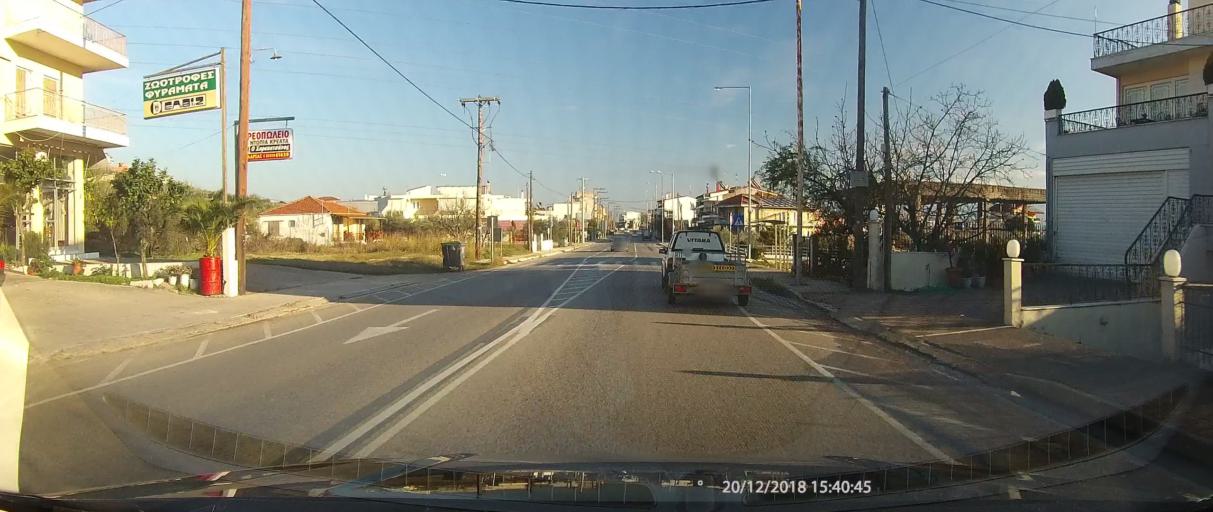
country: GR
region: Central Greece
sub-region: Nomos Fthiotidos
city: Stavros
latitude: 38.8922
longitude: 22.3777
